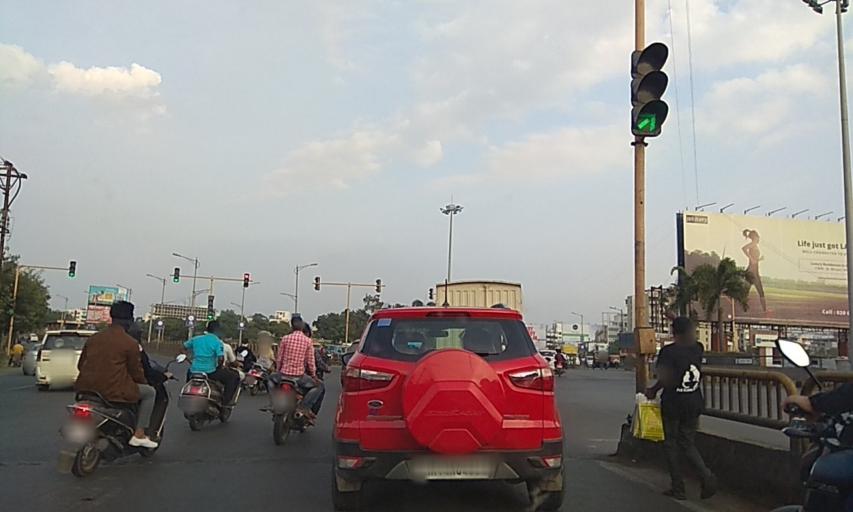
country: IN
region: Maharashtra
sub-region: Pune Division
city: Pimpri
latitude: 18.5891
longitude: 73.7767
